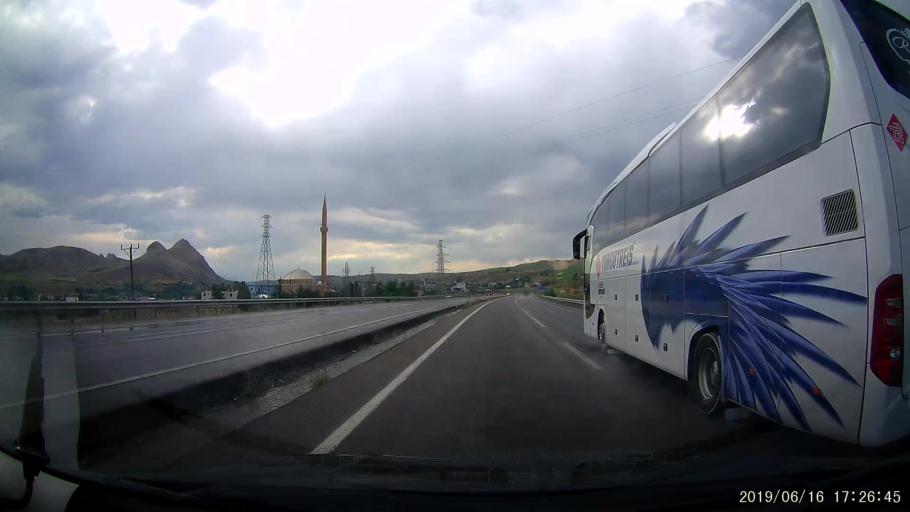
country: TR
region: Erzincan
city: Tercan
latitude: 39.7713
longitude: 40.4058
